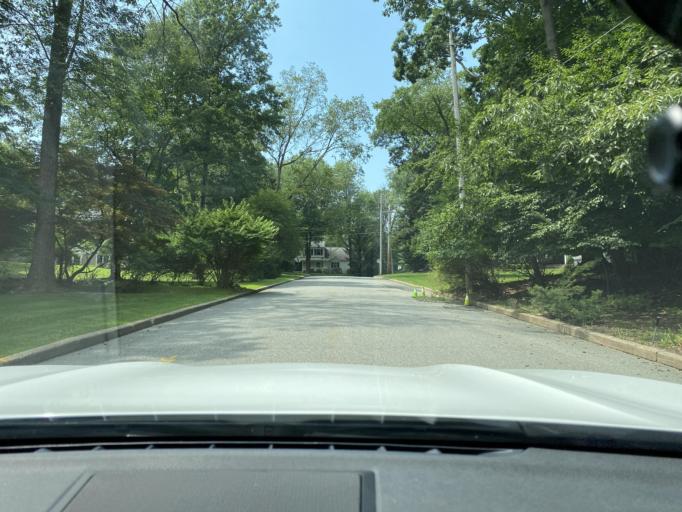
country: US
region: New Jersey
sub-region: Bergen County
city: Upper Saddle River
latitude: 41.0800
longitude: -74.1063
